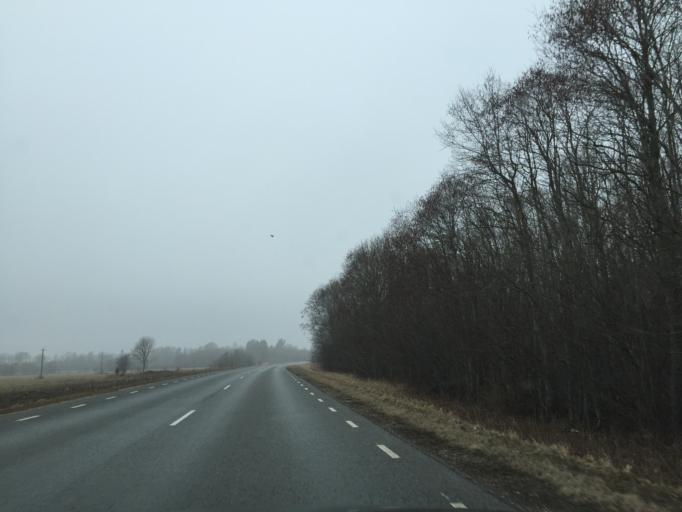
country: EE
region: Laeaene
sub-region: Lihula vald
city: Lihula
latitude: 58.5790
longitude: 23.7265
